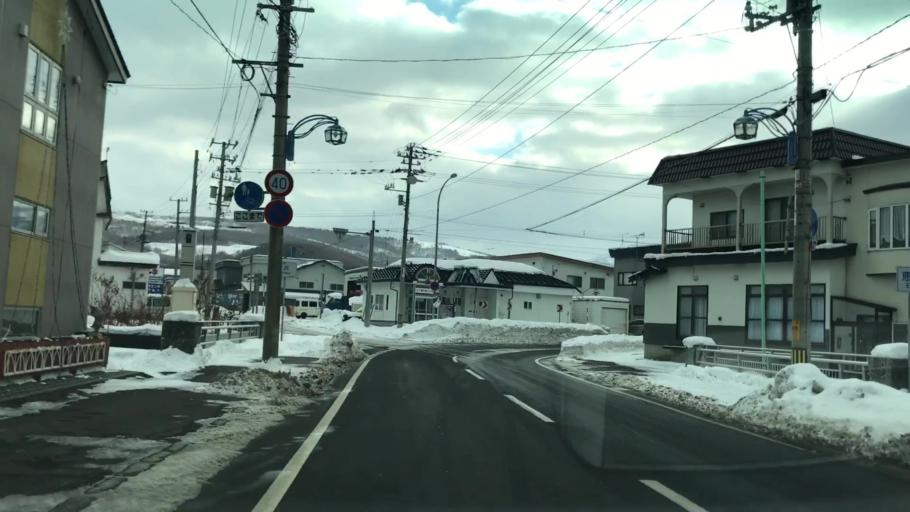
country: JP
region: Hokkaido
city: Yoichi
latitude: 43.2666
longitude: 140.6393
